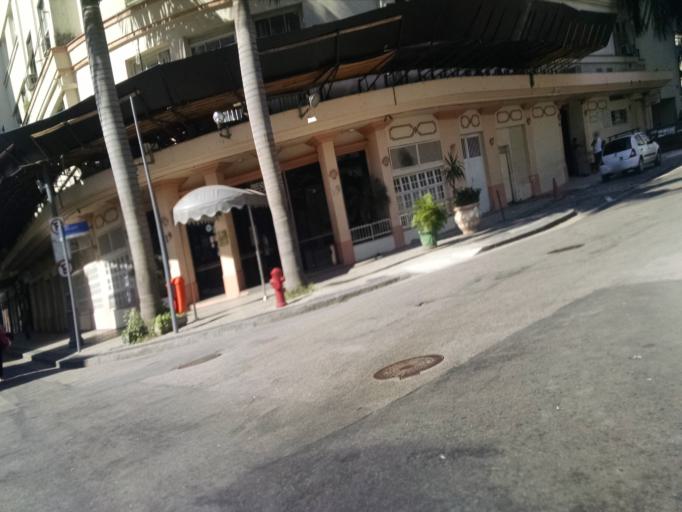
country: BR
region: Rio de Janeiro
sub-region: Rio De Janeiro
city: Rio de Janeiro
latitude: -22.9081
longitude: -43.1825
